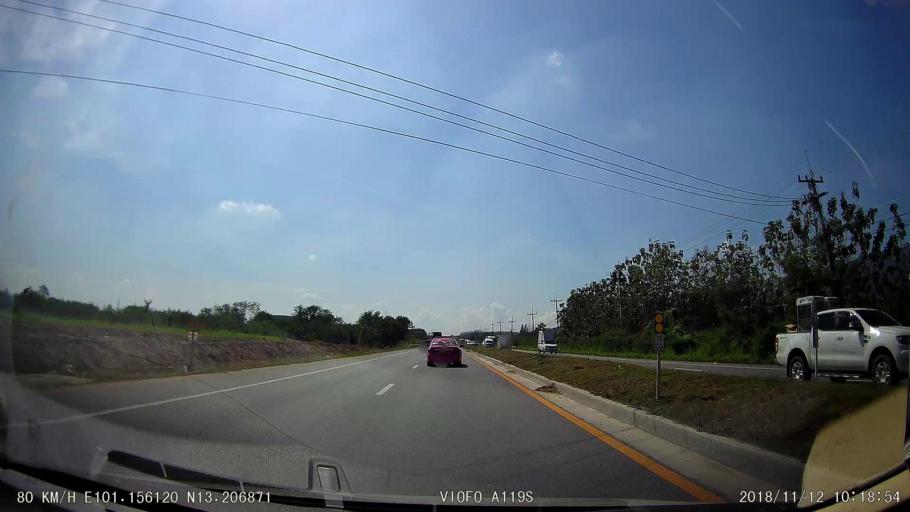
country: TH
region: Chon Buri
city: Ban Bueng
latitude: 13.2064
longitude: 101.1562
